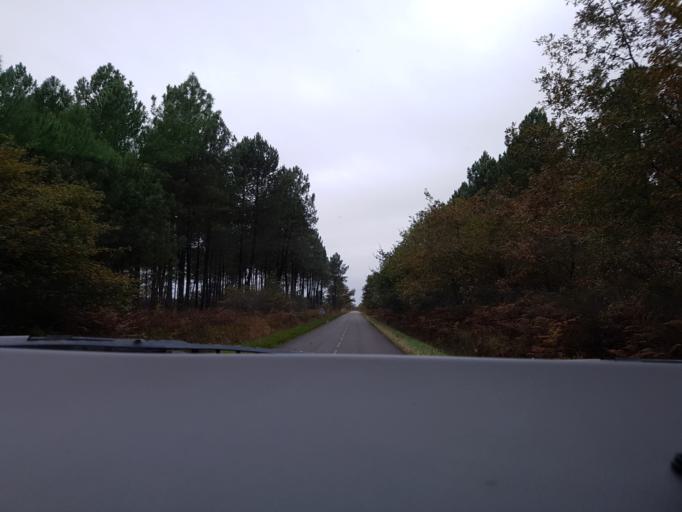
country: FR
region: Aquitaine
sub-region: Departement des Landes
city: Roquefort
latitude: 44.0819
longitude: -0.3816
